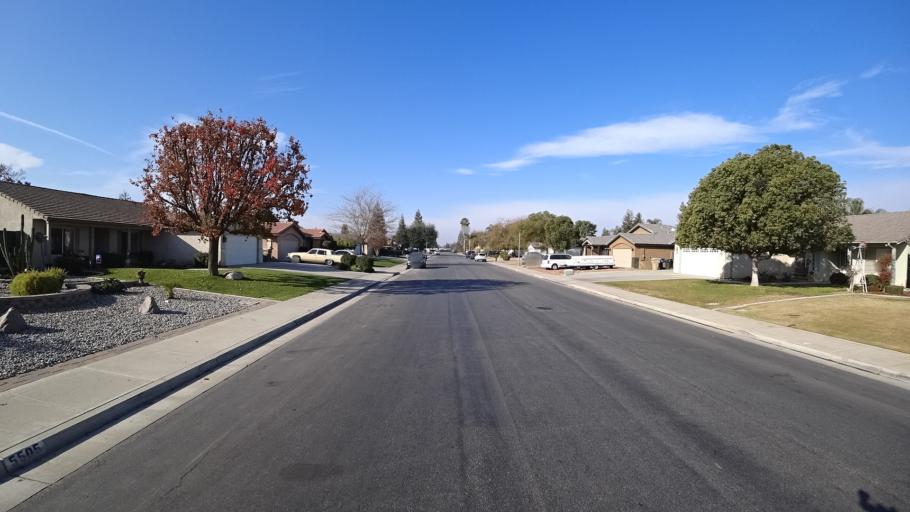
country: US
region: California
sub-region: Kern County
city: Oildale
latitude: 35.4081
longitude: -119.0635
